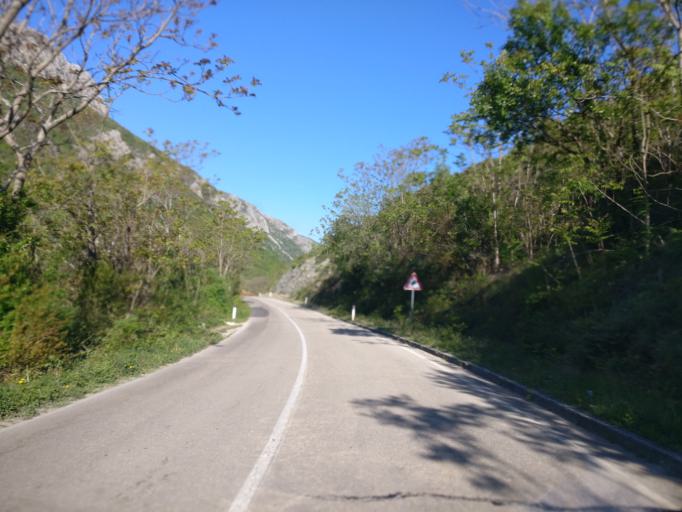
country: BA
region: Federation of Bosnia and Herzegovina
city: Stolac
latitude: 43.0735
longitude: 18.0330
